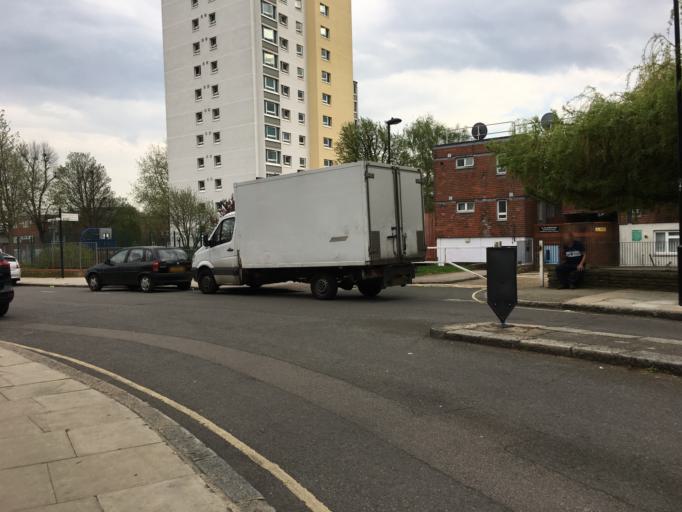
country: GB
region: England
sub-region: Greater London
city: Camden Town
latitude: 51.5494
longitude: -0.1502
